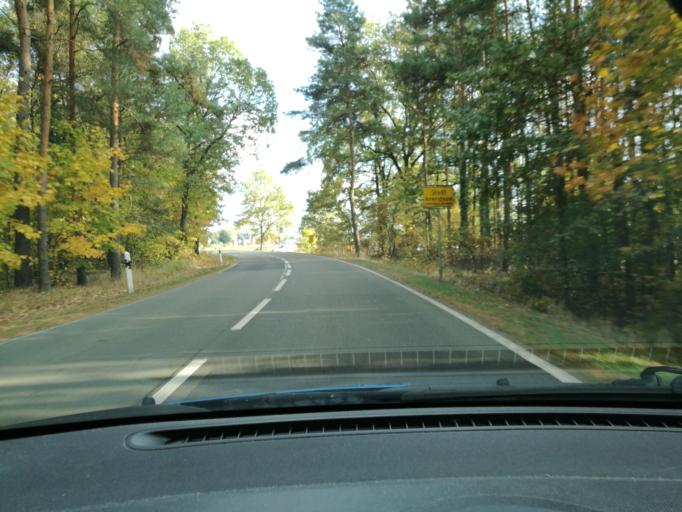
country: DE
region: Saxony-Anhalt
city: Luftkurort Arendsee
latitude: 52.8794
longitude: 11.4550
